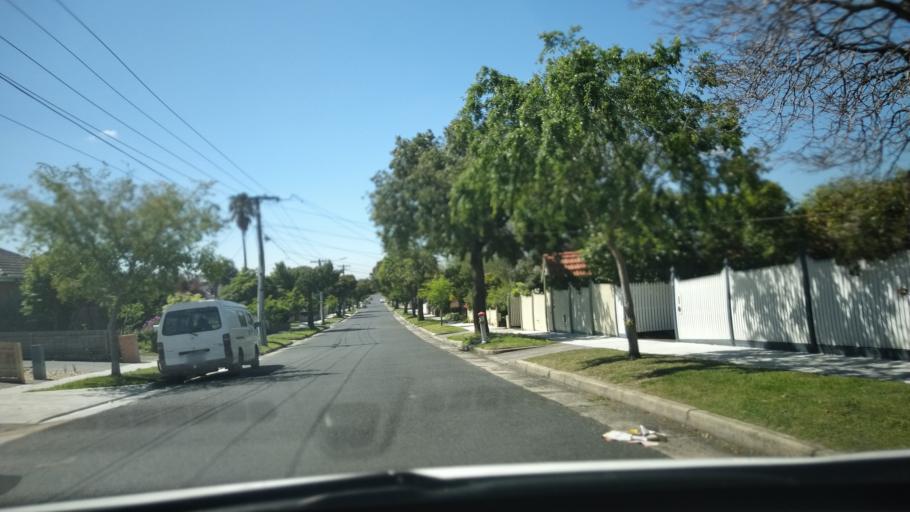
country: AU
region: Victoria
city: Murrumbeena
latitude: -37.9071
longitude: 145.0725
